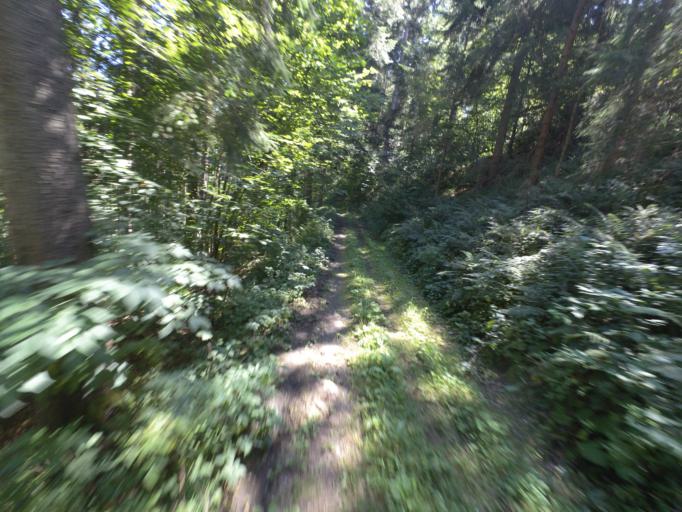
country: AT
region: Salzburg
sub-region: Politischer Bezirk Sankt Johann im Pongau
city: Sankt Veit im Pongau
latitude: 47.3269
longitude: 13.1251
